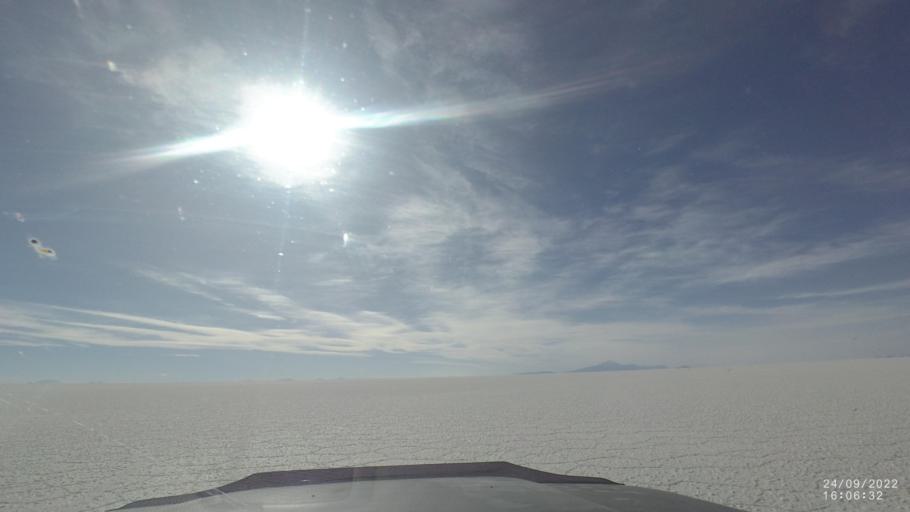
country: BO
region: Potosi
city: Colchani
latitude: -20.3052
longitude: -67.2948
